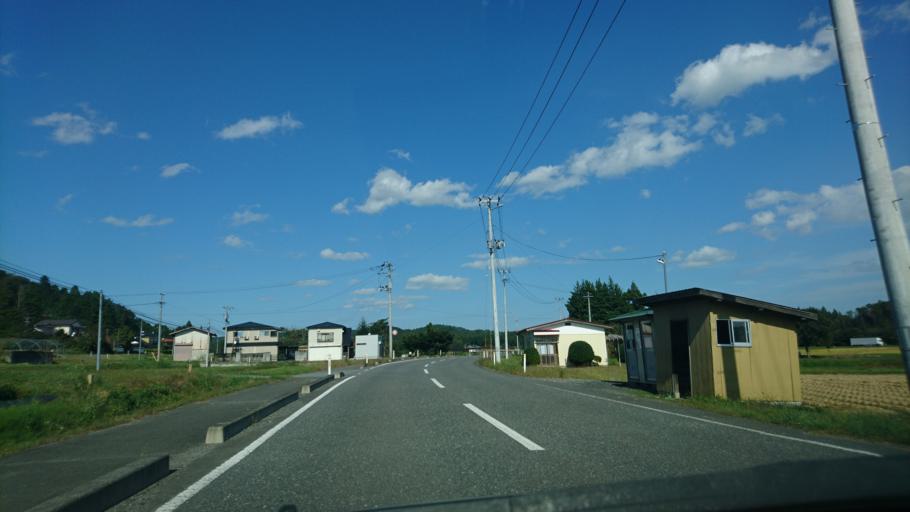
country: JP
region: Iwate
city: Ichinoseki
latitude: 38.8383
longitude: 141.0151
